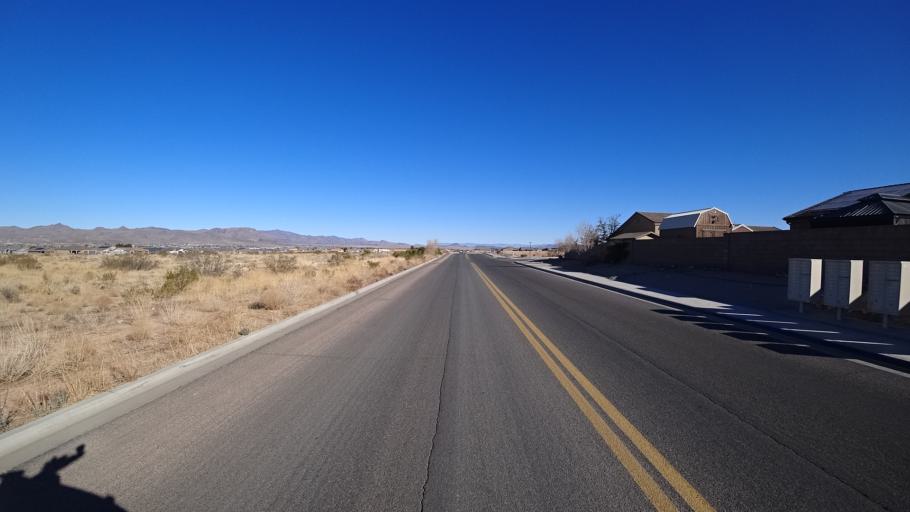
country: US
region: Arizona
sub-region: Mohave County
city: Kingman
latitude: 35.1873
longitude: -114.0027
